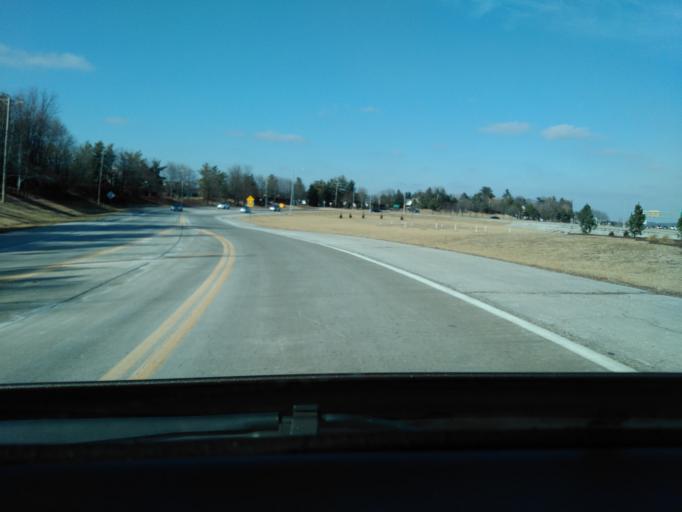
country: US
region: Missouri
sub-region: Saint Louis County
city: Manchester
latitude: 38.6331
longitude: -90.5141
